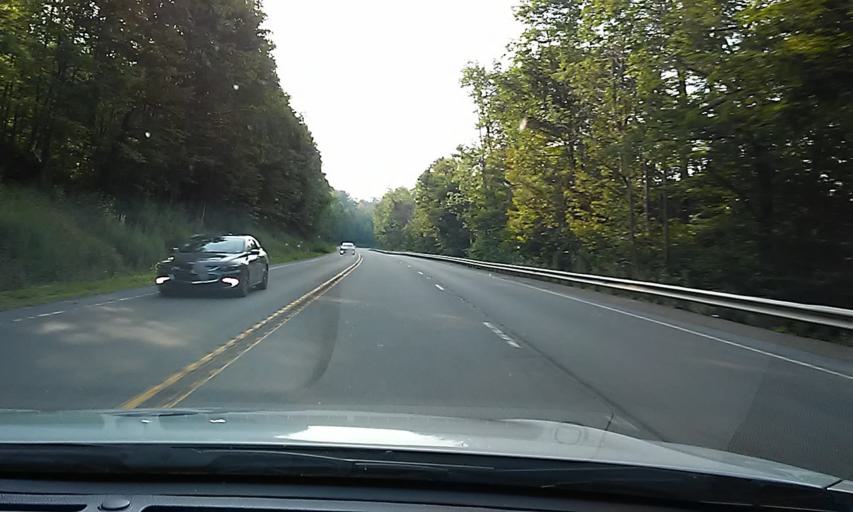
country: US
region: Pennsylvania
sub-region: McKean County
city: Smethport
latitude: 41.7132
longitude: -78.5998
